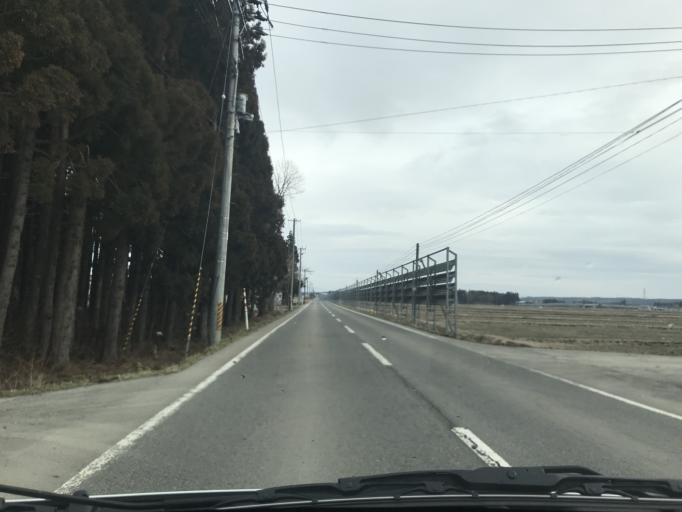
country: JP
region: Iwate
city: Kitakami
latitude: 39.3134
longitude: 141.0206
